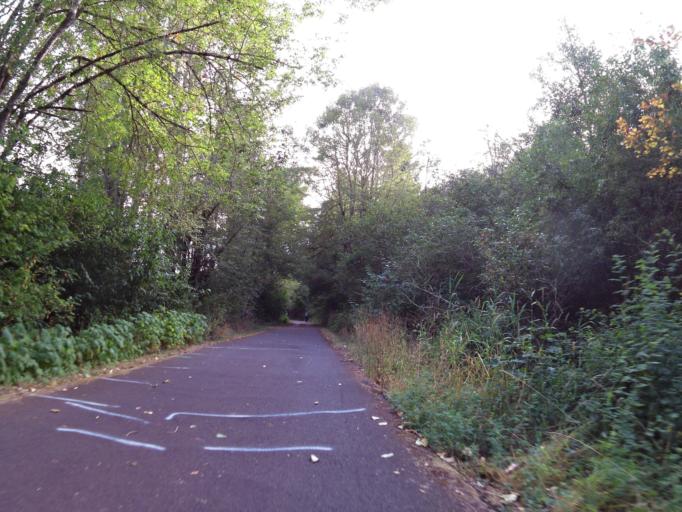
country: US
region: Washington
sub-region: Thurston County
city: Lacey
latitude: 46.9453
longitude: -122.8186
